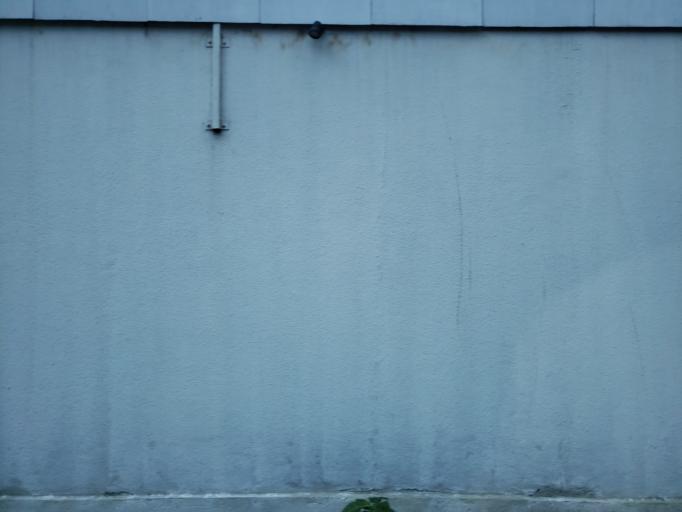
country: ID
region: Bali
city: Kuta
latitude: -8.6831
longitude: 115.1708
